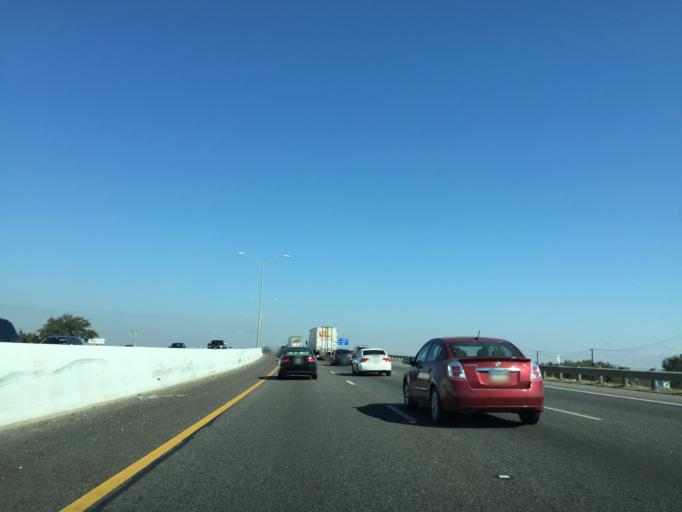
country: US
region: Texas
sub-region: Williamson County
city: Georgetown
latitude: 30.6049
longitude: -97.6866
